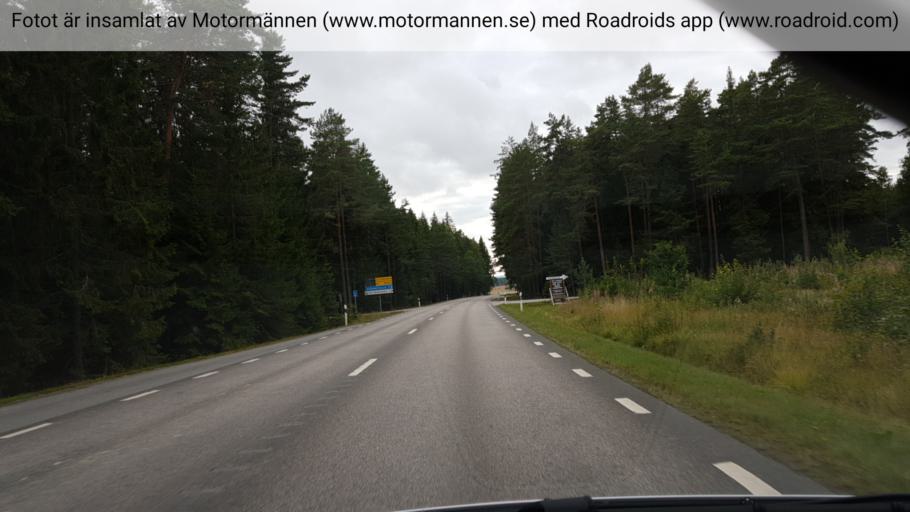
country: SE
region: Vaestra Goetaland
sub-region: Tibro Kommun
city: Tibro
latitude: 58.3433
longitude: 14.1569
